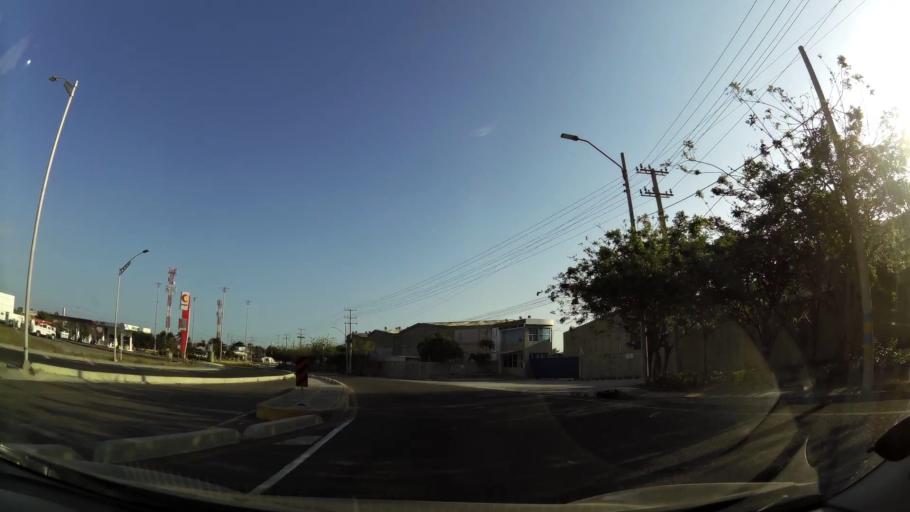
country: CO
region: Atlantico
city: Barranquilla
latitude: 11.0373
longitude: -74.8270
